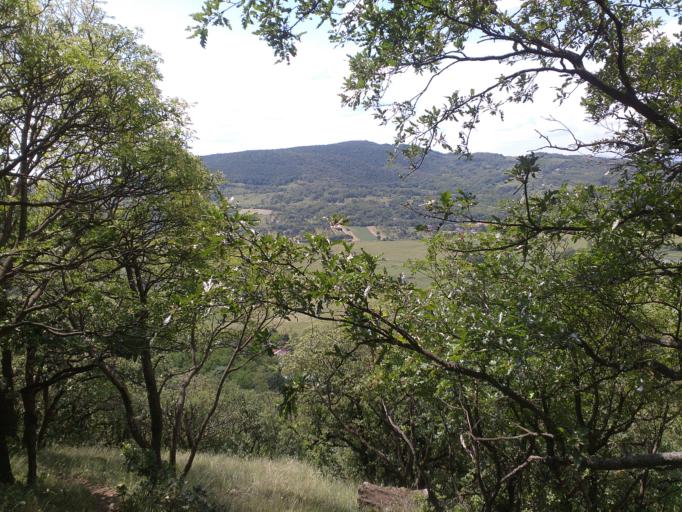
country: HU
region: Komarom-Esztergom
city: Esztergom
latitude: 47.8067
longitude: 18.7975
